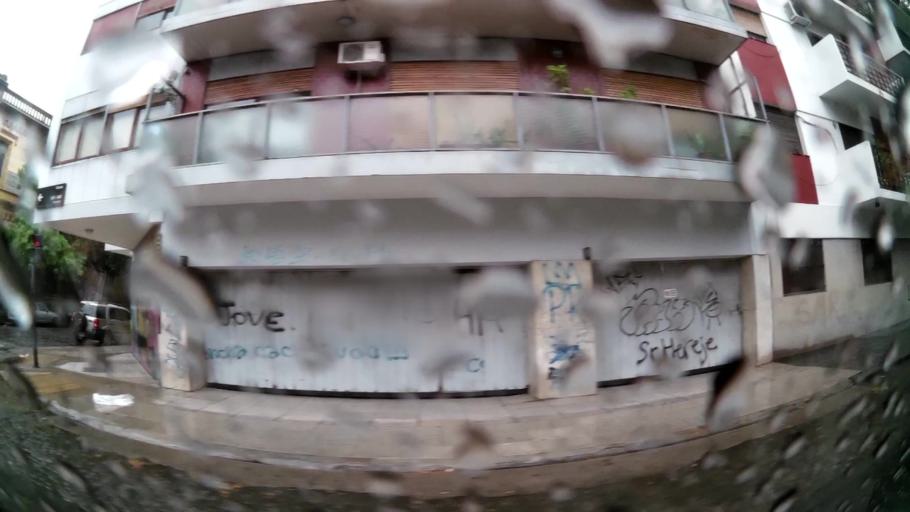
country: AR
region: Buenos Aires F.D.
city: Buenos Aires
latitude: -34.6365
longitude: -58.3717
